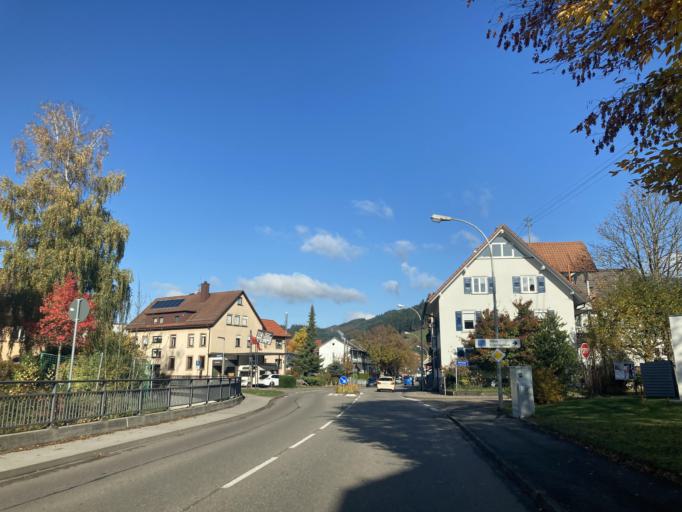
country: DE
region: Baden-Wuerttemberg
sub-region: Freiburg Region
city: Hofstetten
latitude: 48.2741
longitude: 8.0904
